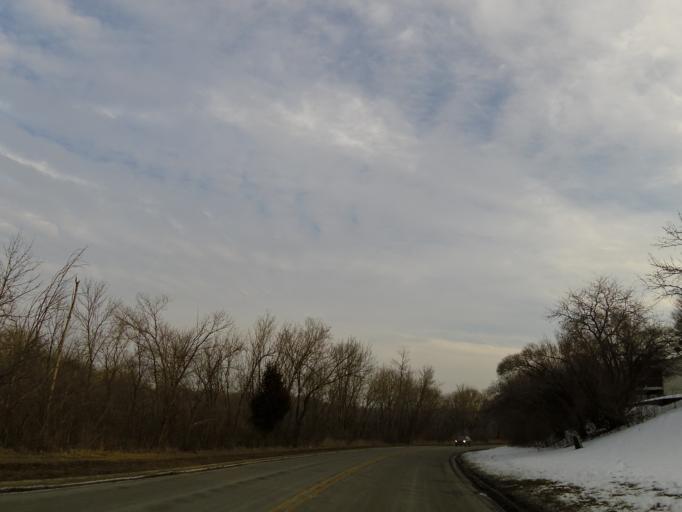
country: US
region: Minnesota
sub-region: Hennepin County
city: Eden Prairie
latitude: 44.8410
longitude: -93.4108
